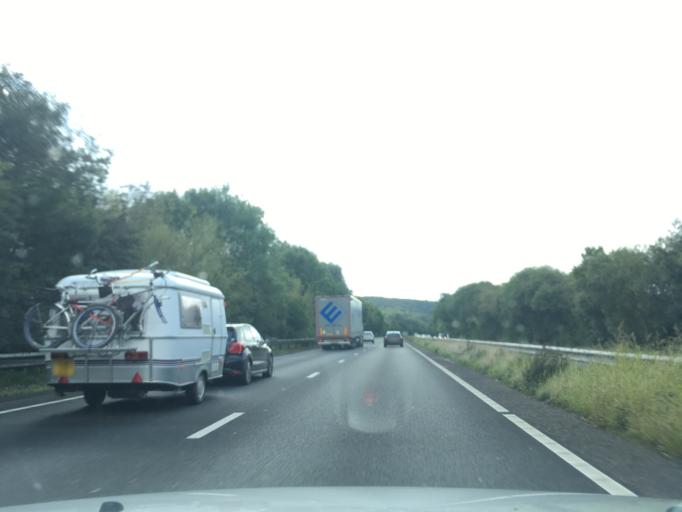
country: GB
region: England
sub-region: Hampshire
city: Petersfield
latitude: 50.9931
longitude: -0.9542
